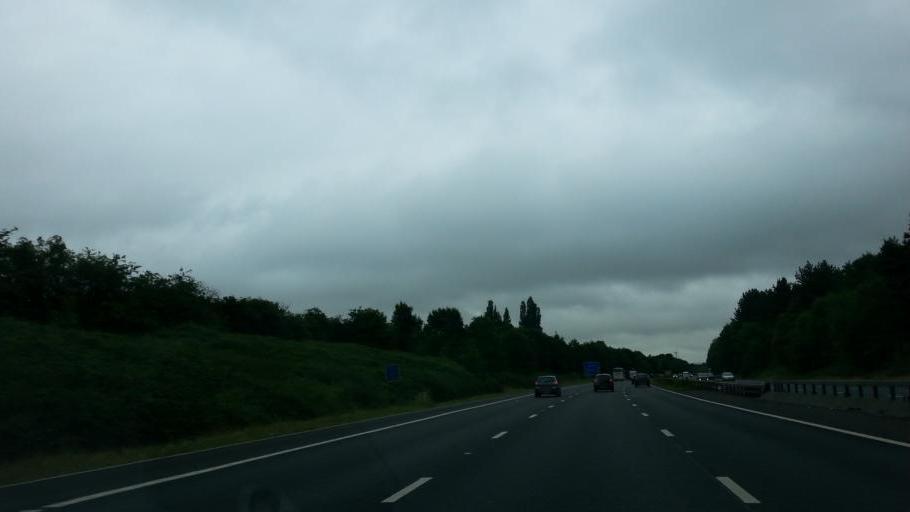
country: GB
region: England
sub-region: Leicestershire
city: Cosby
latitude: 52.5255
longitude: -1.1754
